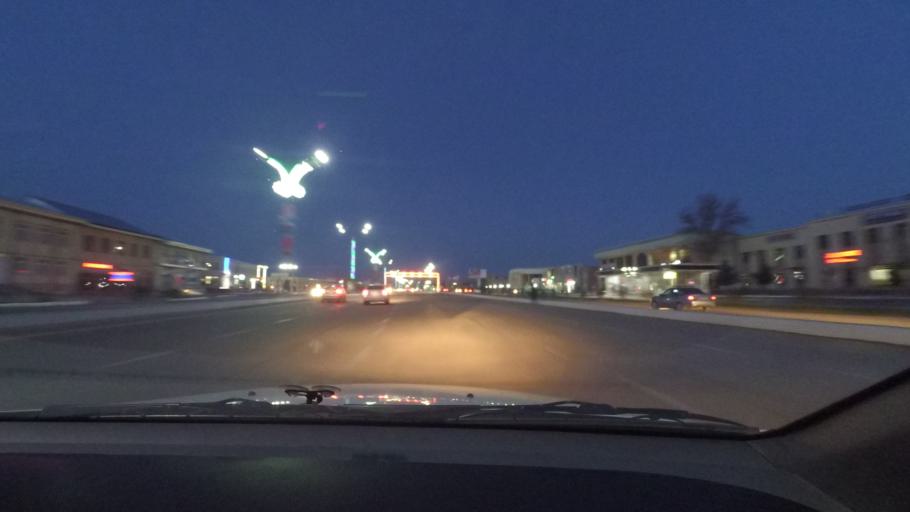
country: UZ
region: Bukhara
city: Bukhara
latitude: 39.7836
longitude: 64.4185
